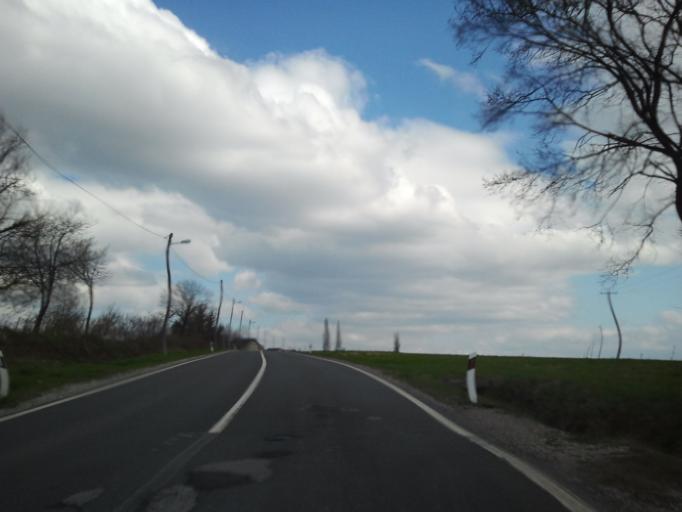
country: HR
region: Grad Zagreb
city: Horvati
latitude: 45.7029
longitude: 15.7705
